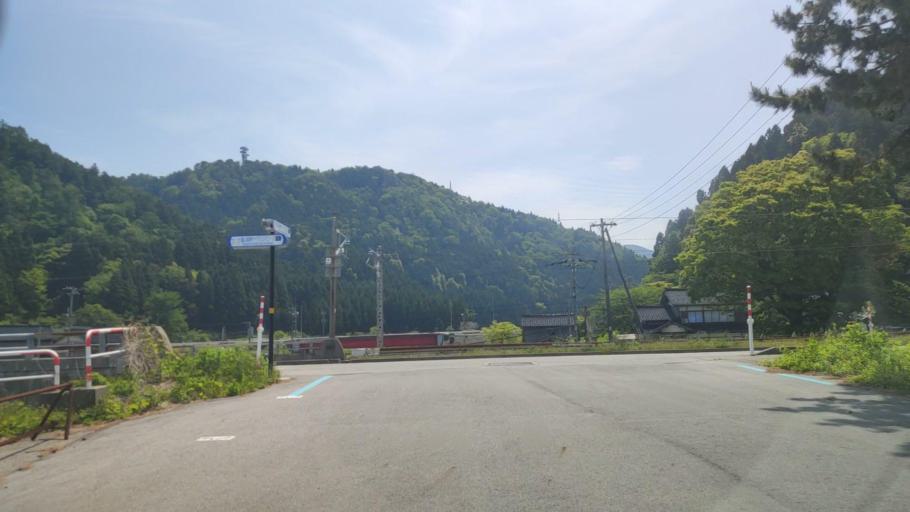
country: JP
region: Toyama
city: Nyuzen
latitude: 36.9637
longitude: 137.5743
